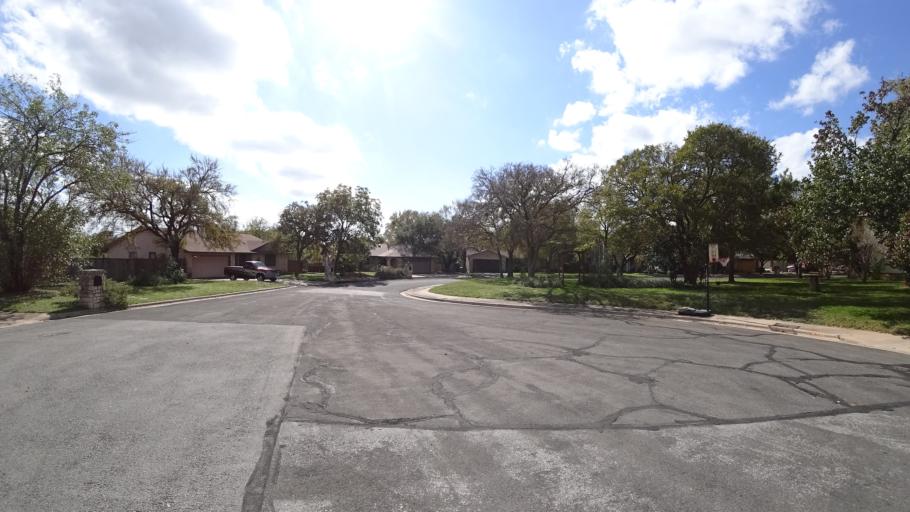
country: US
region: Texas
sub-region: Travis County
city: Wells Branch
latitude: 30.4128
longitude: -97.7220
